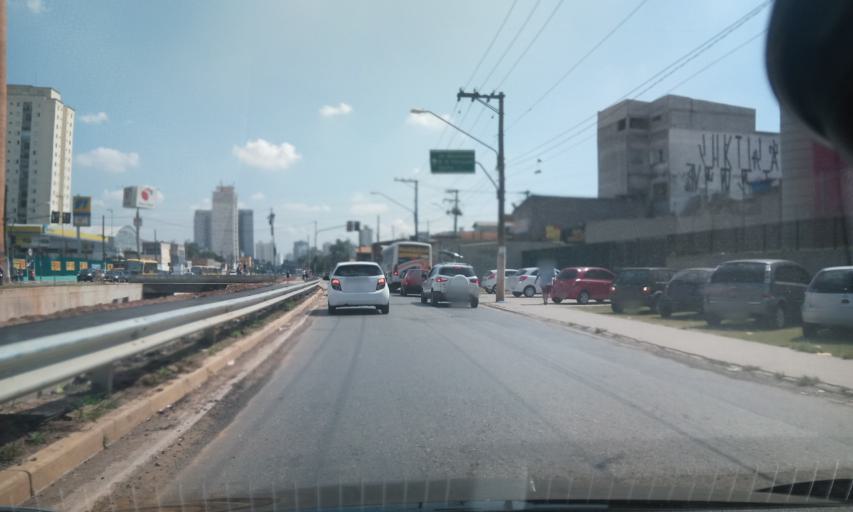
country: BR
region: Sao Paulo
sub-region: Sao Bernardo Do Campo
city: Sao Bernardo do Campo
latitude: -23.7066
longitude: -46.5337
